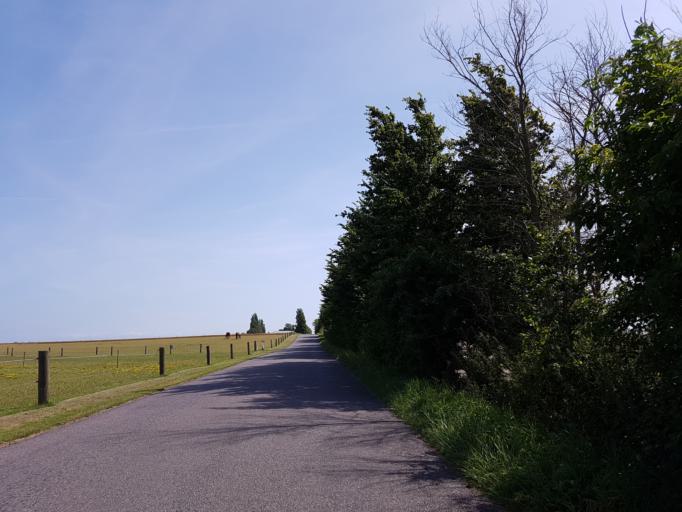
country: DK
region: Zealand
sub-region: Guldborgsund Kommune
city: Nykobing Falster
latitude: 54.5854
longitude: 11.9410
